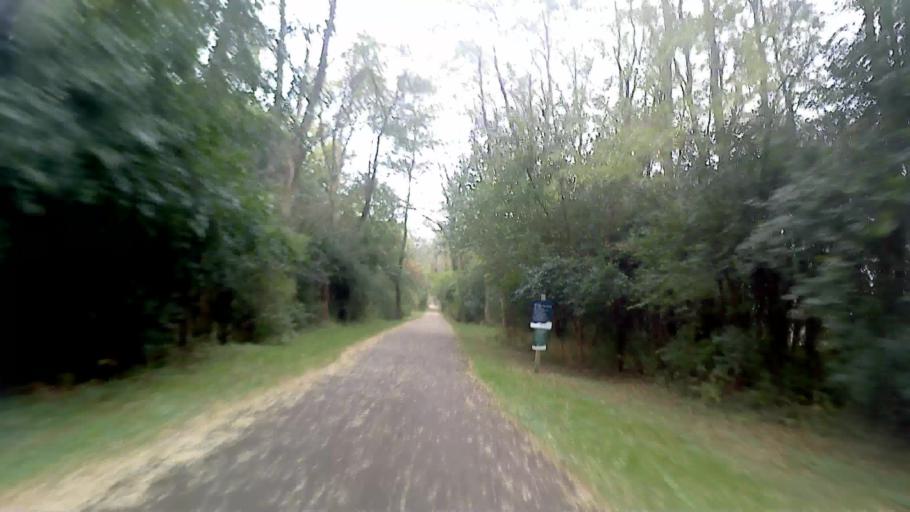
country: US
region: Illinois
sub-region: Kane County
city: Sugar Grove
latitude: 41.7721
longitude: -88.4108
